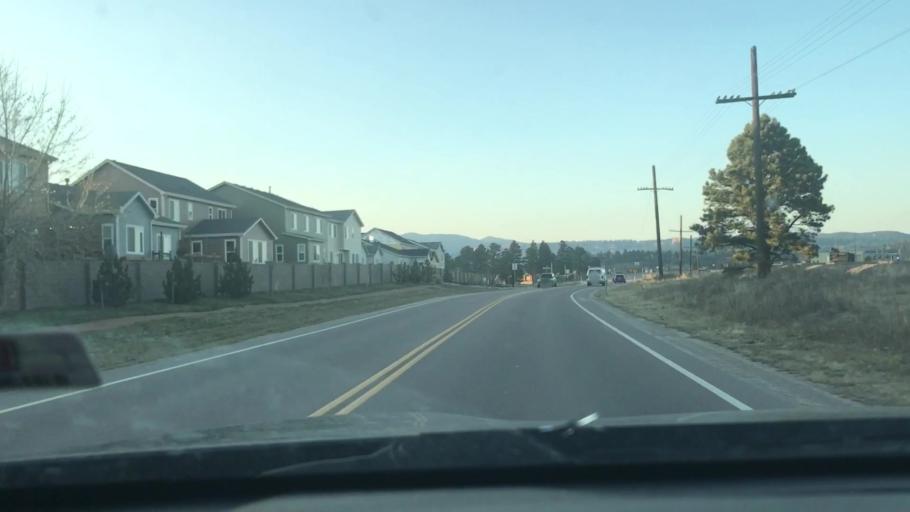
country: US
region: Colorado
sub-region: El Paso County
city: Monument
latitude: 39.0881
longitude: -104.8742
